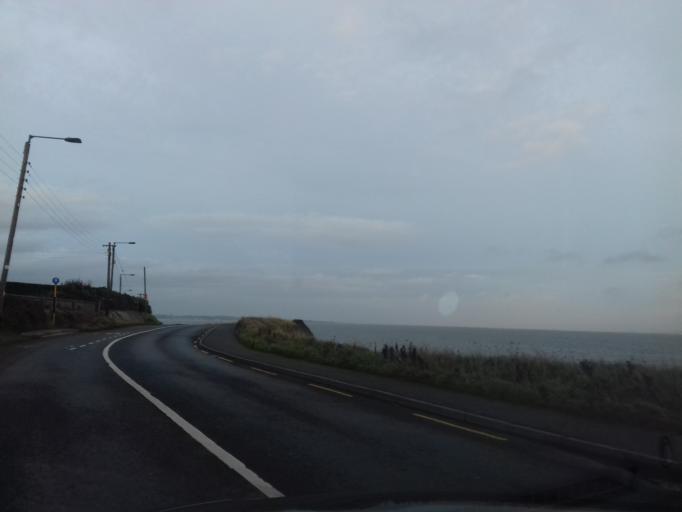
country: IE
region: Leinster
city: Portmarnock
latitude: 53.4384
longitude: -6.1230
